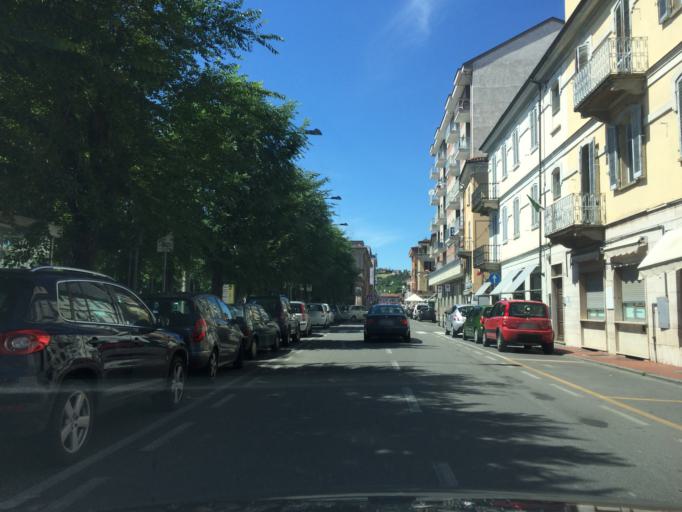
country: IT
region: Piedmont
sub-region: Provincia di Asti
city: Nizza Monferrato
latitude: 44.7730
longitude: 8.3548
